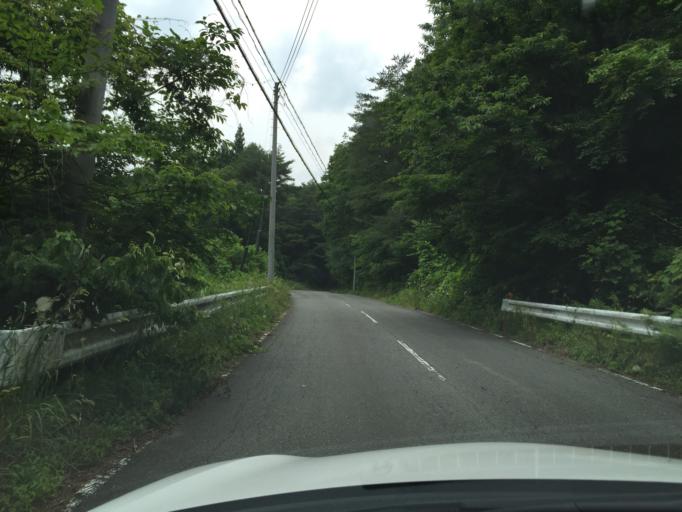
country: JP
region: Fukushima
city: Iwaki
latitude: 37.1532
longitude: 140.7005
